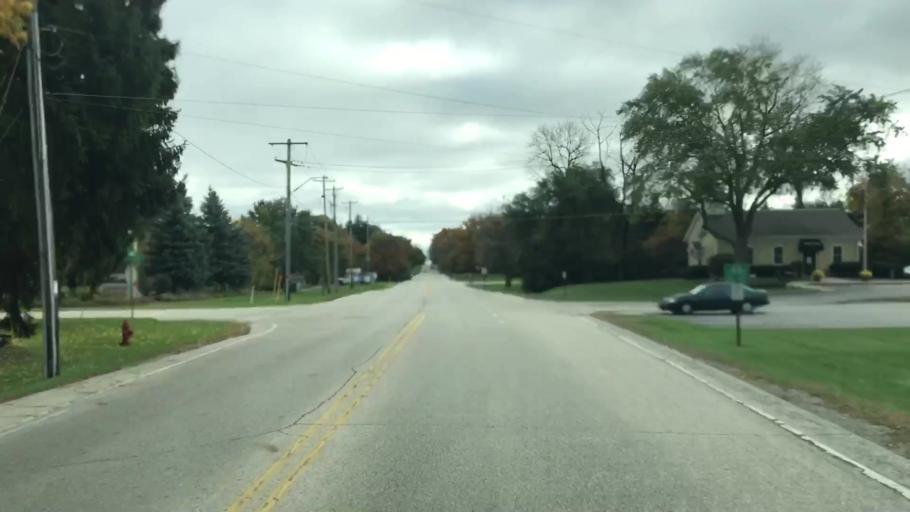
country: US
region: Wisconsin
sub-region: Waukesha County
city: Brookfield
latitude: 43.0605
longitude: -88.1067
